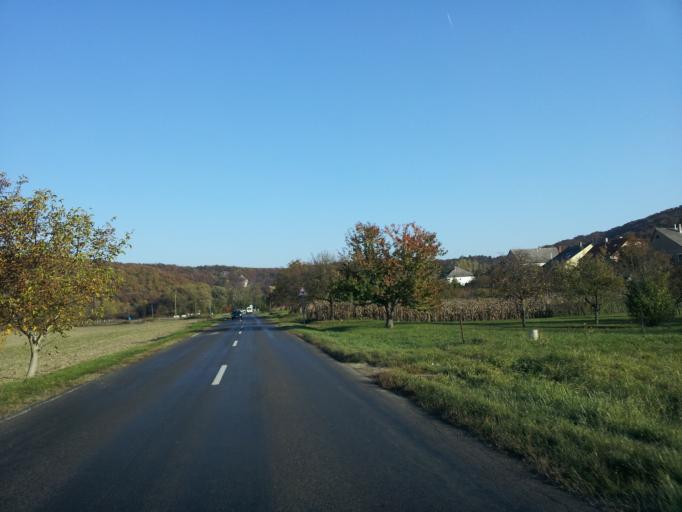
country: HU
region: Fejer
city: Bodajk
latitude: 47.3146
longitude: 18.2013
